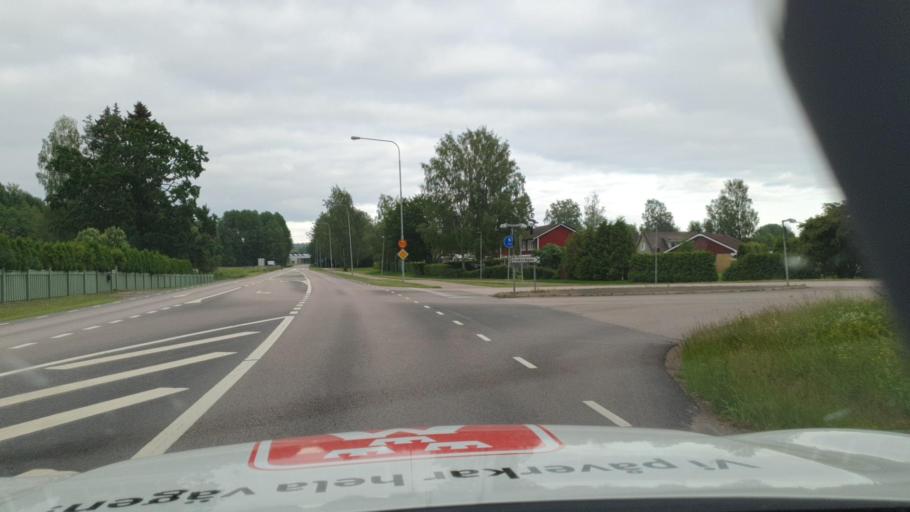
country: SE
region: Vaermland
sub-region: Forshaga Kommun
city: Forshaga
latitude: 59.4492
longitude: 13.4281
